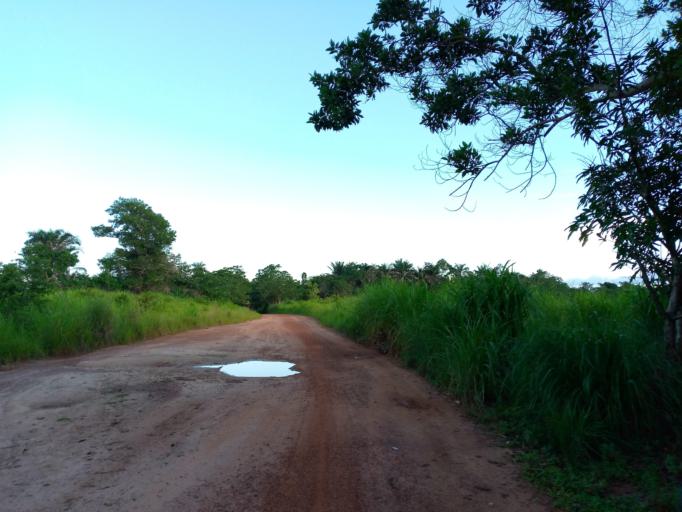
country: SL
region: Northern Province
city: Yonibana
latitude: 8.4569
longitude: -12.2470
